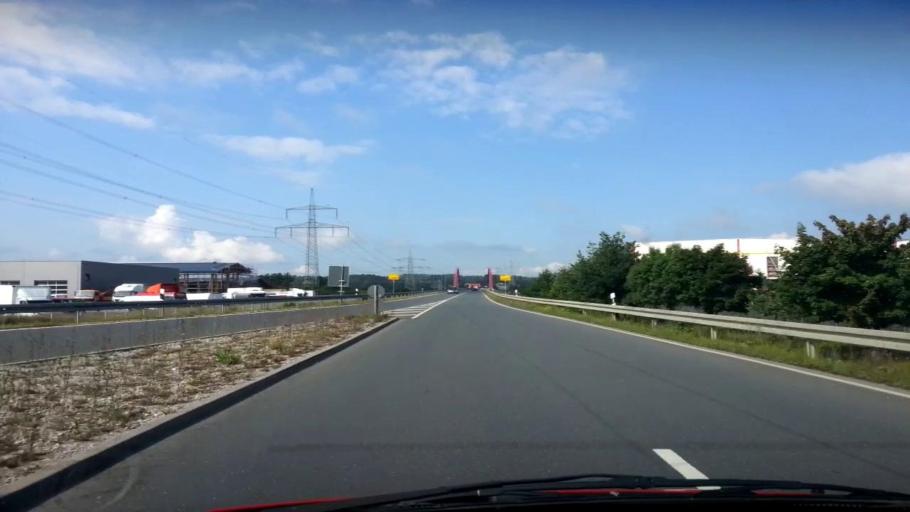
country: DE
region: Bavaria
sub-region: Upper Franconia
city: Hausen
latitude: 49.7001
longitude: 11.0448
